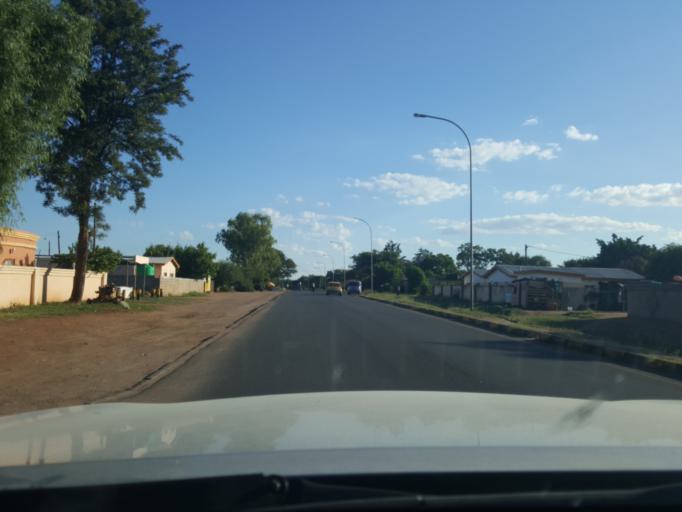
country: BW
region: South East
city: Gaborone
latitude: -24.6298
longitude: 25.9415
